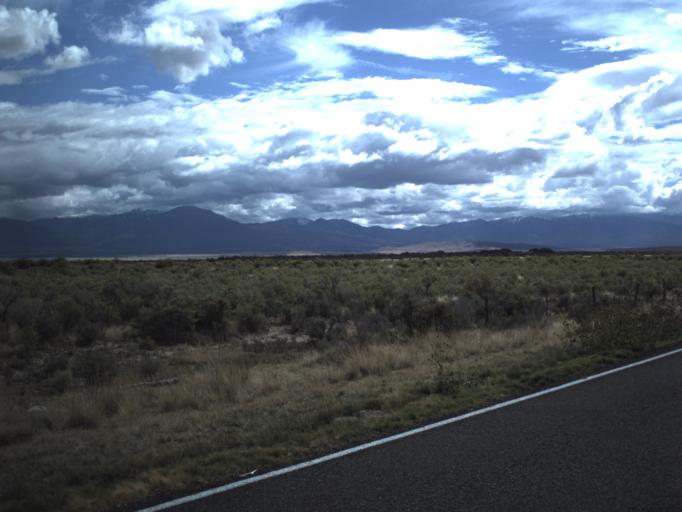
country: US
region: Utah
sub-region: Millard County
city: Fillmore
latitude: 39.1486
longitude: -112.4099
